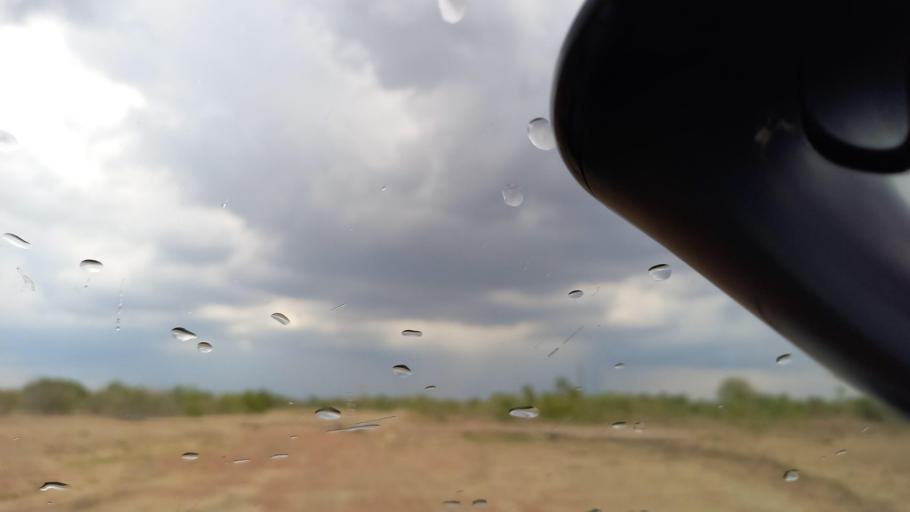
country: ZM
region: Lusaka
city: Kafue
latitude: -15.8555
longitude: 28.1148
